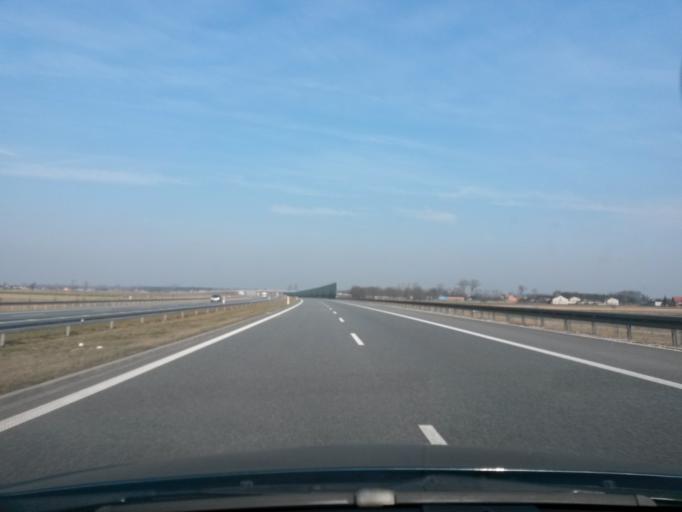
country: PL
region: Lodz Voivodeship
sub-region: Powiat leczycki
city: Piatek
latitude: 52.0773
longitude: 19.5320
